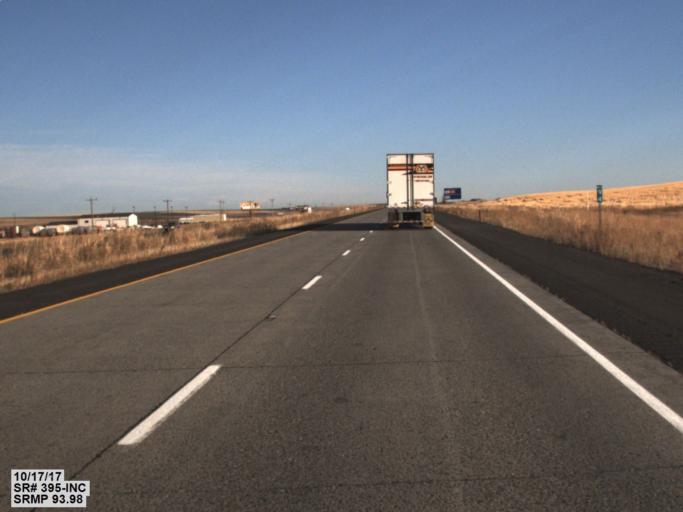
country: US
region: Washington
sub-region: Adams County
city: Ritzville
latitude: 47.0879
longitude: -118.4103
